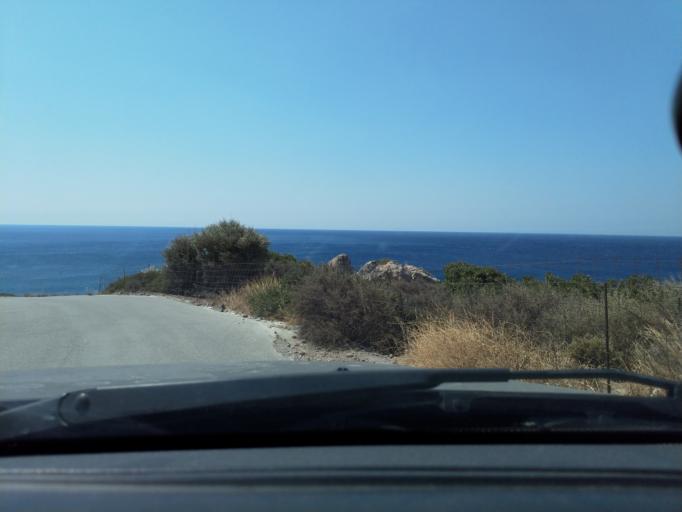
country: GR
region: Crete
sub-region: Nomos Rethymnis
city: Agia Foteini
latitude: 35.1397
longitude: 24.5285
